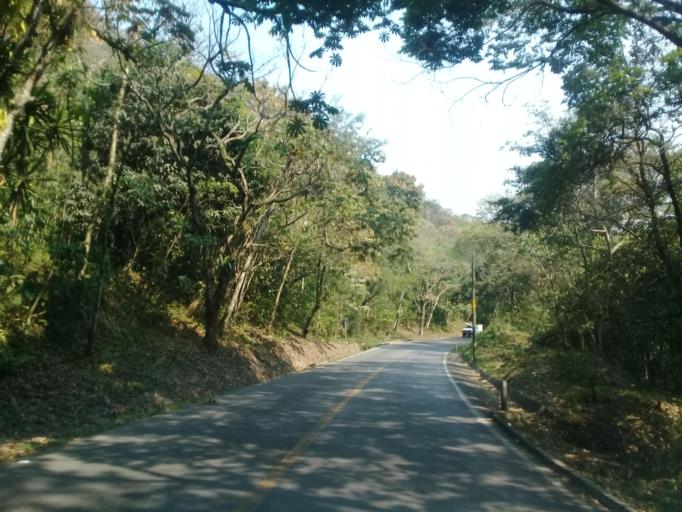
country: MX
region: Veracruz
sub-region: Ixtaczoquitlan
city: Campo Chico
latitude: 18.8448
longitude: -97.0306
